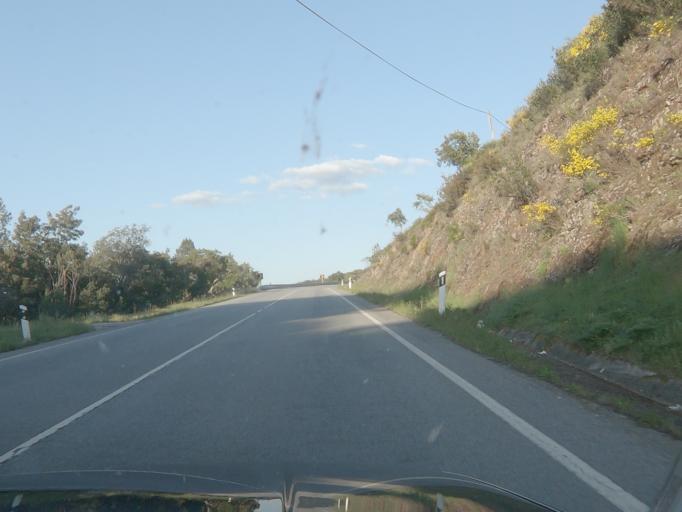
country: PT
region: Portalegre
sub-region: Portalegre
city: Sao Juliao
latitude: 39.3634
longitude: -7.3249
